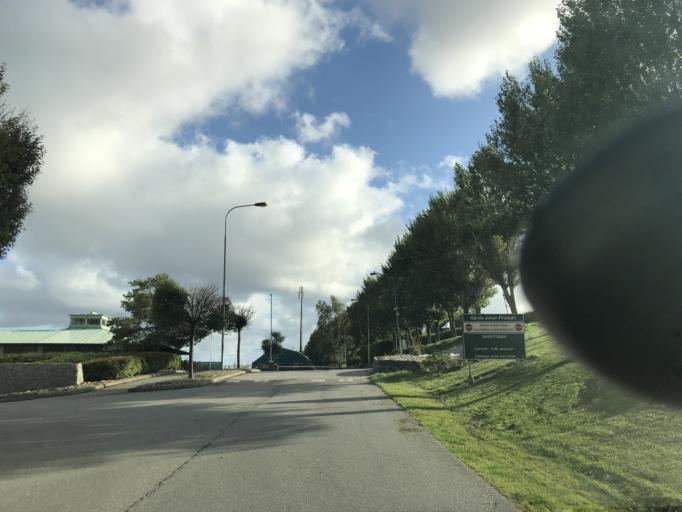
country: SE
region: Vaestra Goetaland
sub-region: Goteborg
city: Goeteborg
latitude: 57.7414
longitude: 11.9460
